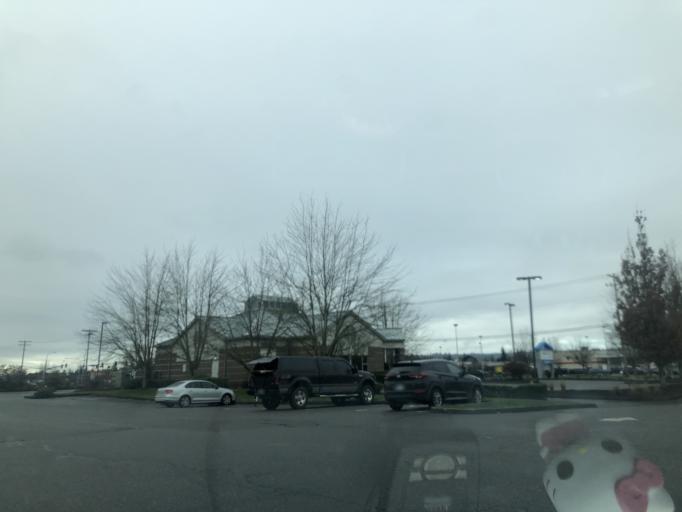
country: US
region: Washington
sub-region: Snohomish County
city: Smokey Point
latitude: 48.1517
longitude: -122.1819
